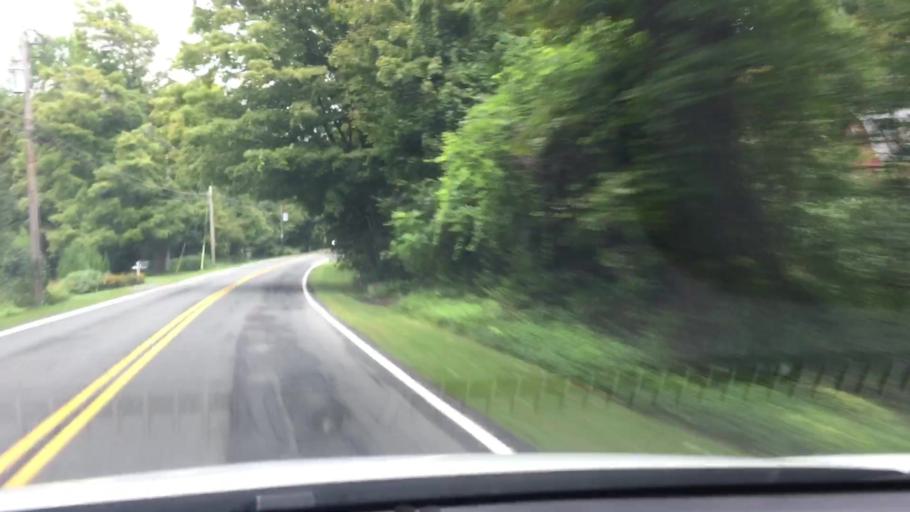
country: US
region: Massachusetts
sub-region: Berkshire County
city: Housatonic
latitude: 42.2396
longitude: -73.3729
